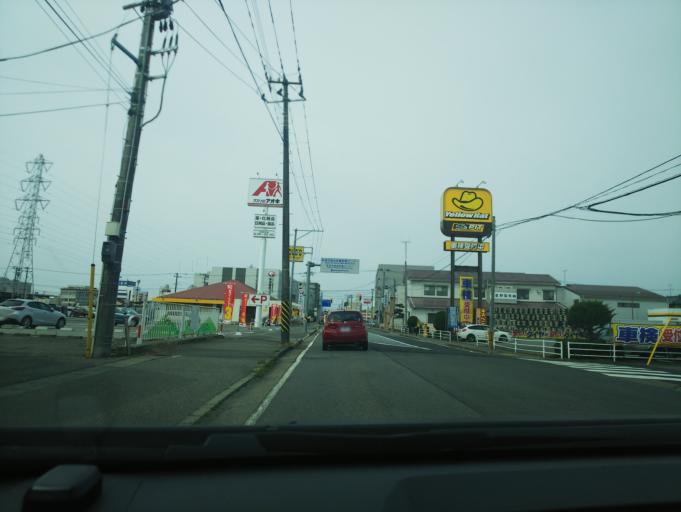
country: JP
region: Niigata
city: Niigata-shi
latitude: 37.9021
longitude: 139.0700
